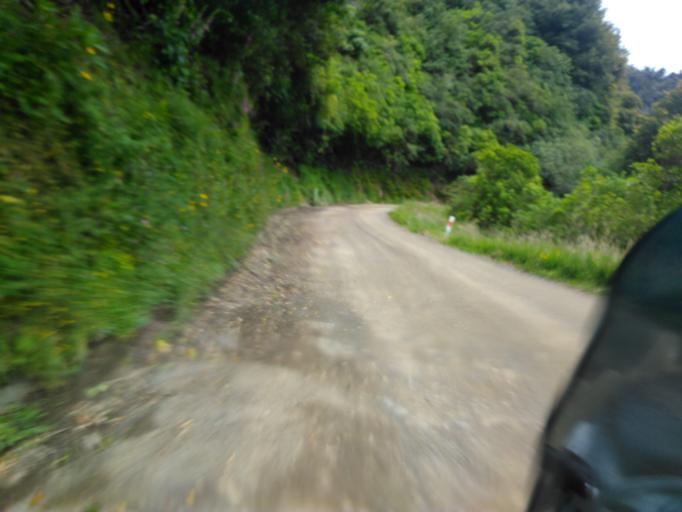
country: NZ
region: Bay of Plenty
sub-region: Opotiki District
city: Opotiki
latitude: -38.0890
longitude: 177.4803
